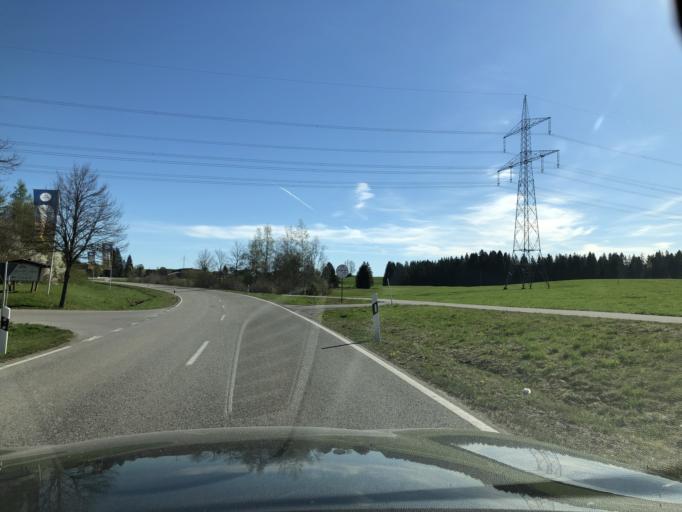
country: DE
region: Bavaria
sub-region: Swabia
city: Nesselwang
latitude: 47.6313
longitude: 10.5178
